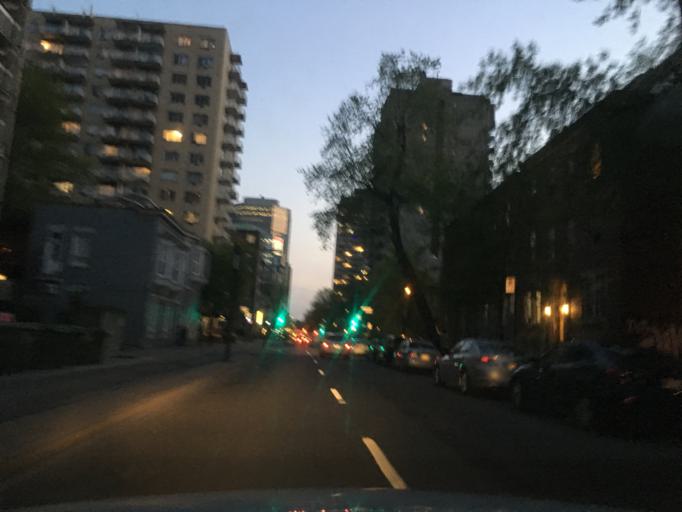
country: CA
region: Quebec
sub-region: Montreal
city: Montreal
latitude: 45.4923
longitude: -73.5833
